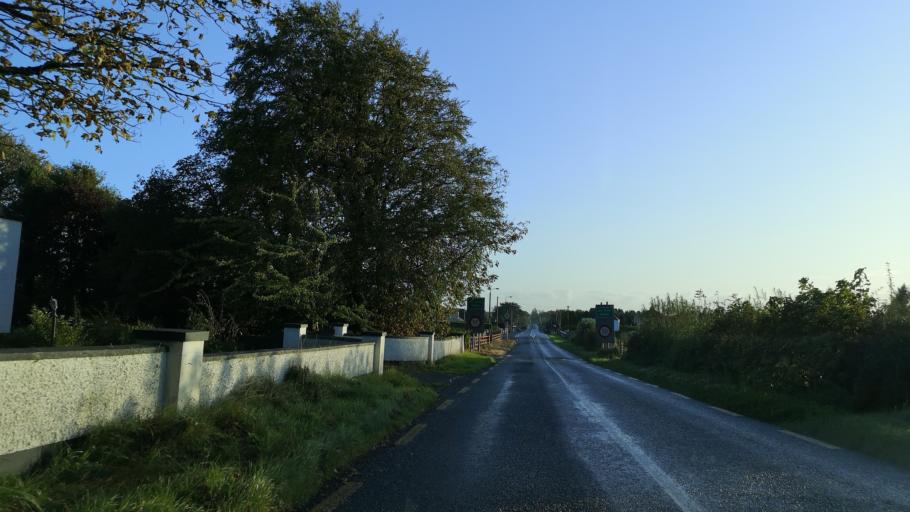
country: IE
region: Connaught
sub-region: Roscommon
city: Castlerea
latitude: 53.7355
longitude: -8.5511
